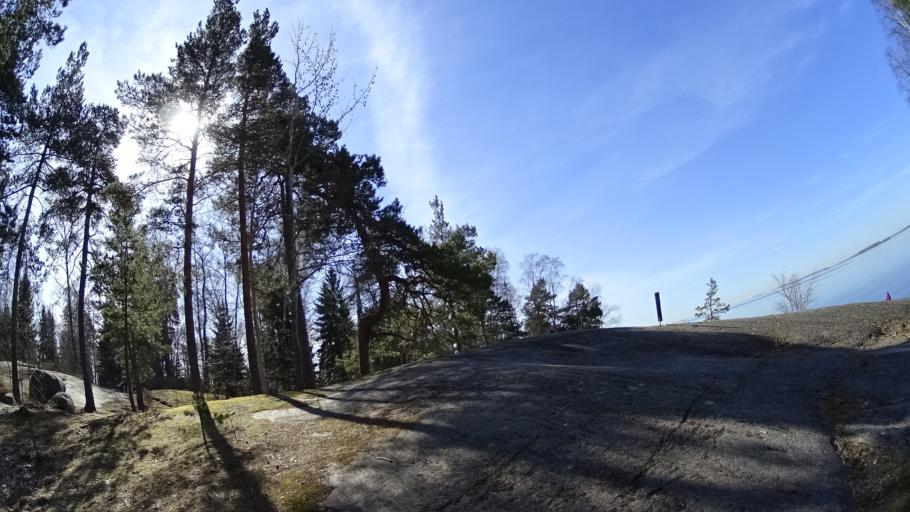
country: FI
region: Uusimaa
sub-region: Helsinki
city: Teekkarikylae
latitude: 60.1458
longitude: 24.8726
